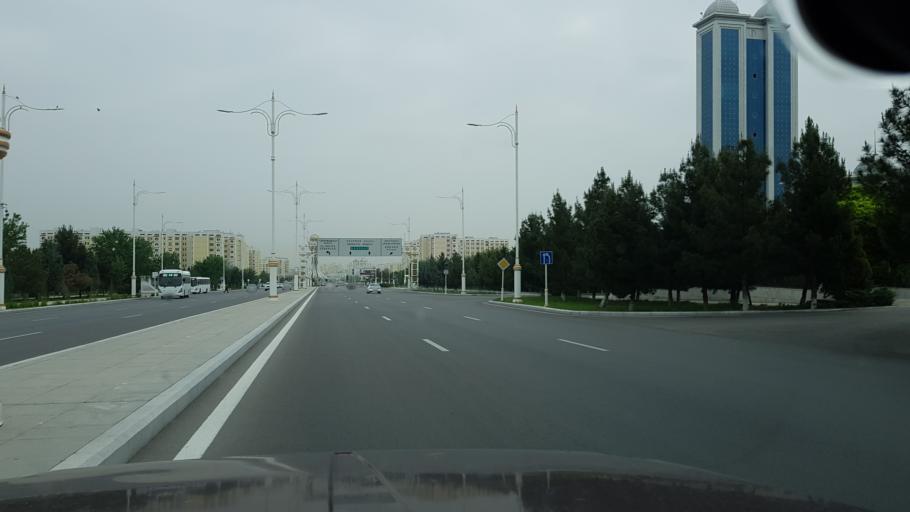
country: TM
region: Ahal
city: Ashgabat
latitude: 37.8923
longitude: 58.3881
